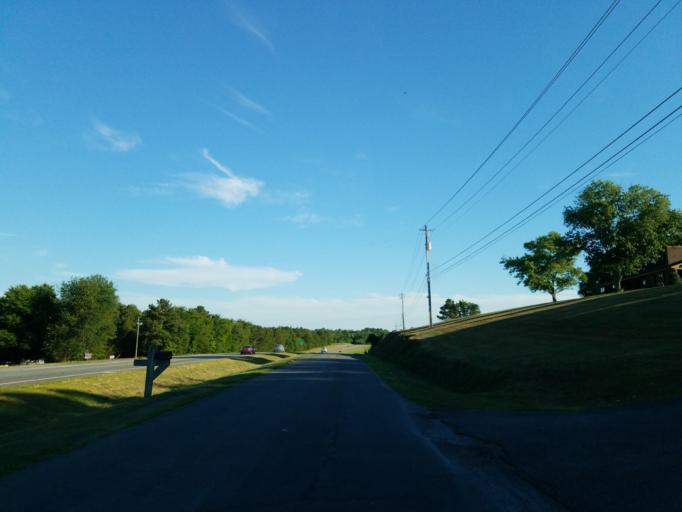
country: US
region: Georgia
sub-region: Bartow County
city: Adairsville
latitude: 34.3923
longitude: -84.9345
